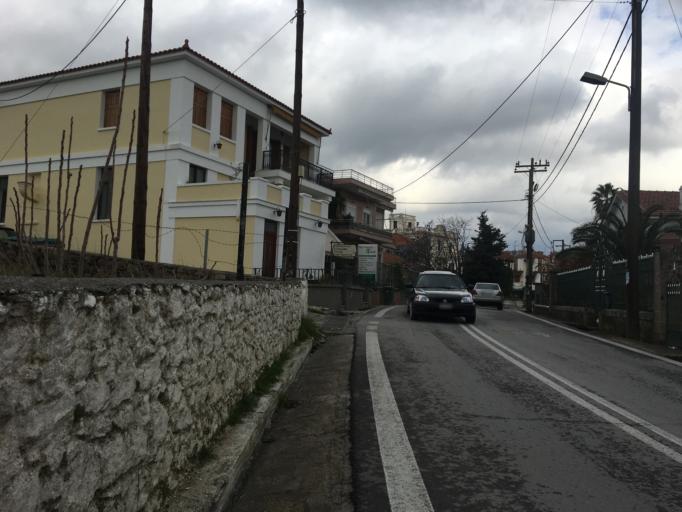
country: GR
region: North Aegean
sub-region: Nomos Lesvou
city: Agia Paraskevi
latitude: 39.2455
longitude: 26.2690
